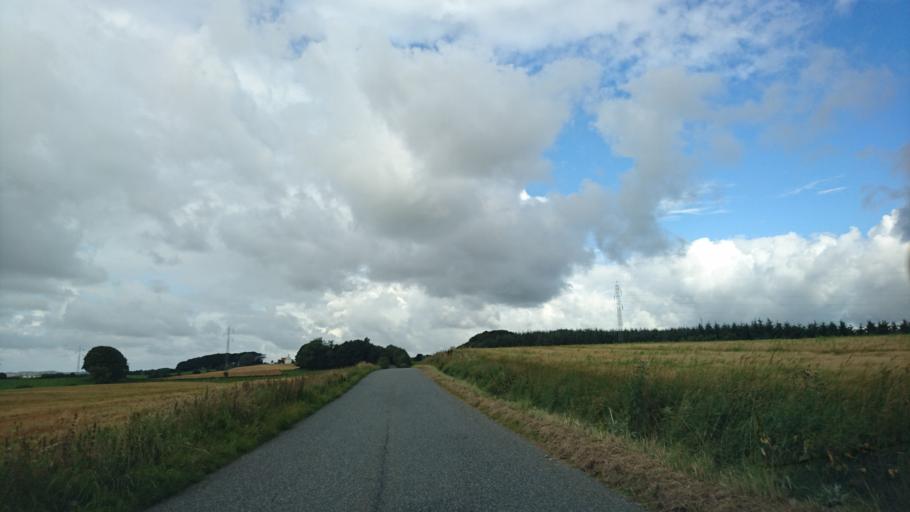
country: DK
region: North Denmark
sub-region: Hjorring Kommune
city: Sindal
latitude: 57.3784
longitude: 10.2420
